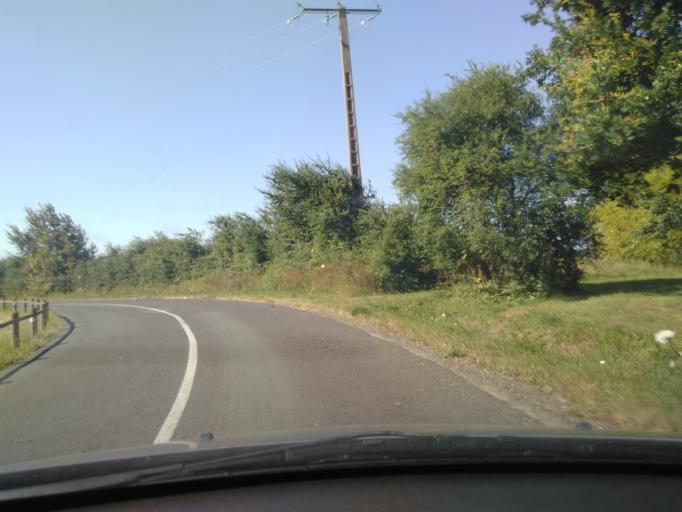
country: FR
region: Pays de la Loire
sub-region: Departement de la Vendee
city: Mouilleron-le-Captif
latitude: 46.7308
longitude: -1.4205
